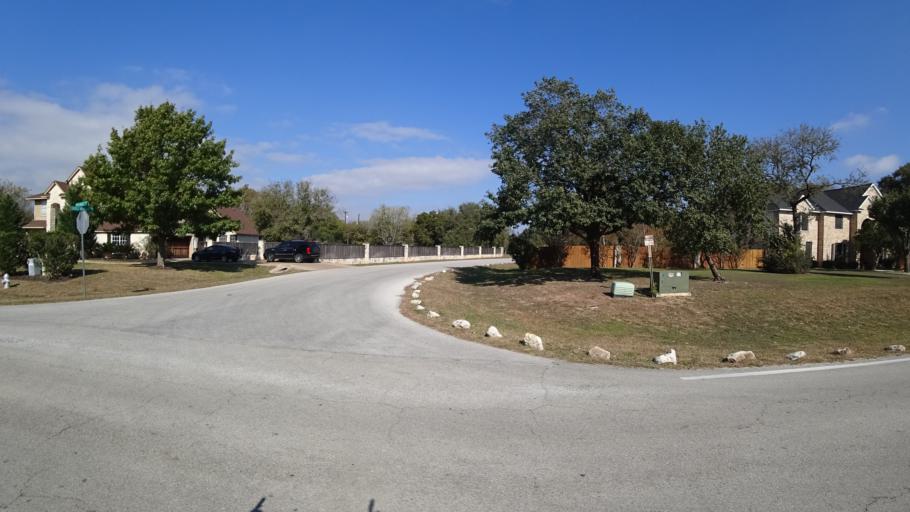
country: US
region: Texas
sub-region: Travis County
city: Shady Hollow
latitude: 30.1615
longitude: -97.8623
